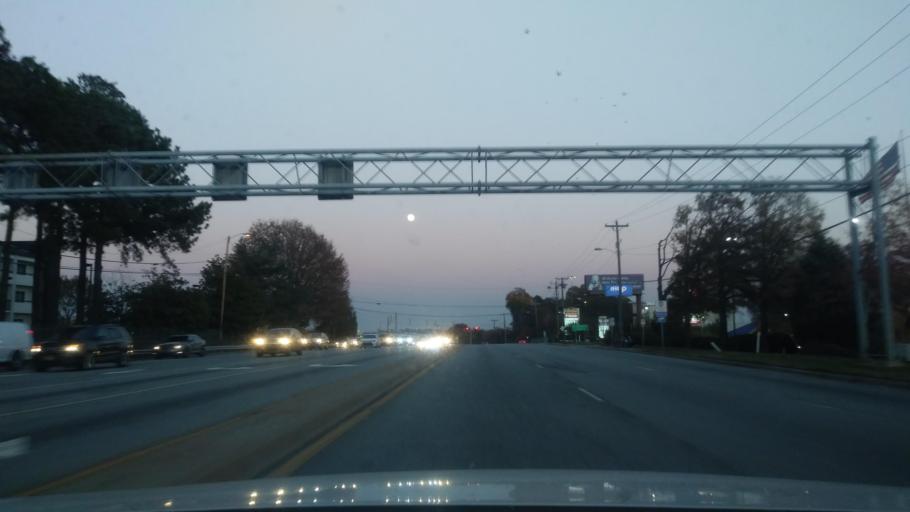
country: US
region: North Carolina
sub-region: Guilford County
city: Jamestown
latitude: 36.0559
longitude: -79.8953
